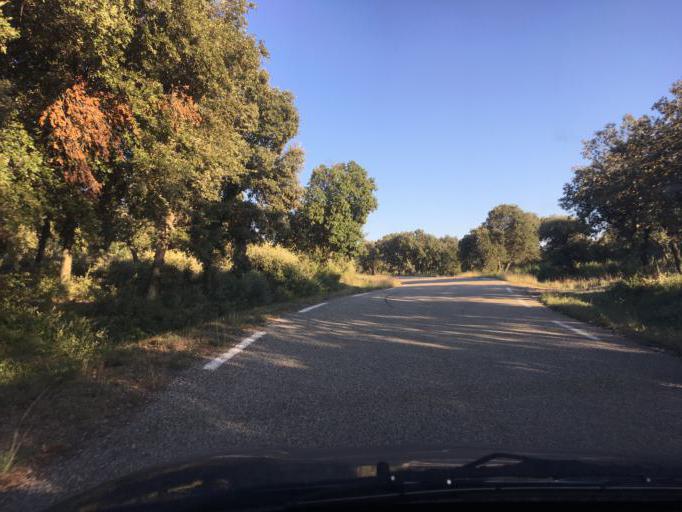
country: FR
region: Languedoc-Roussillon
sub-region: Departement du Gard
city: Saint-Victor-la-Coste
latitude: 44.0087
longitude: 4.6053
